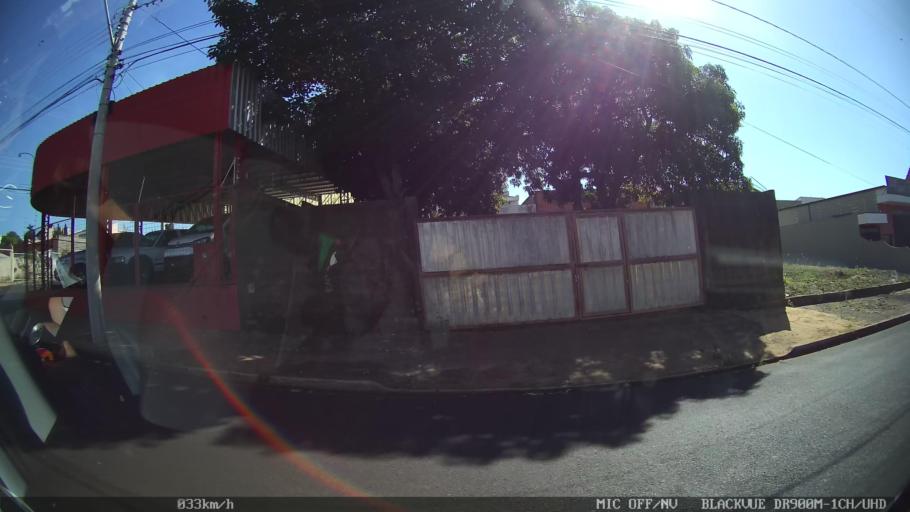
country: BR
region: Sao Paulo
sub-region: Batatais
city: Batatais
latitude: -20.8835
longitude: -47.5969
